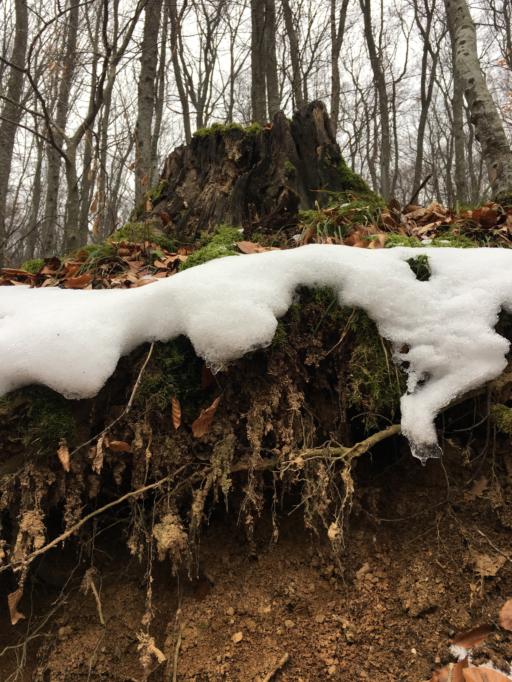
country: XK
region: Pristina
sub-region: Komuna e Prishtines
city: Pristina
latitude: 42.6676
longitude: 21.2262
